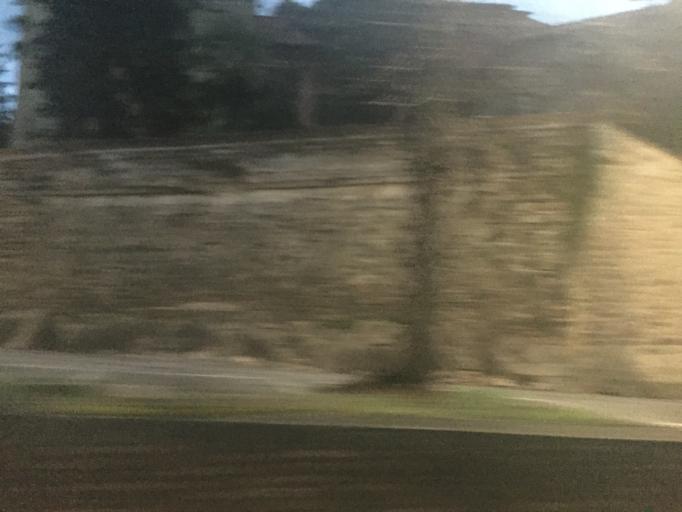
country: IT
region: The Marches
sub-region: Provincia di Macerata
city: Muccia
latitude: 43.0830
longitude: 13.0437
